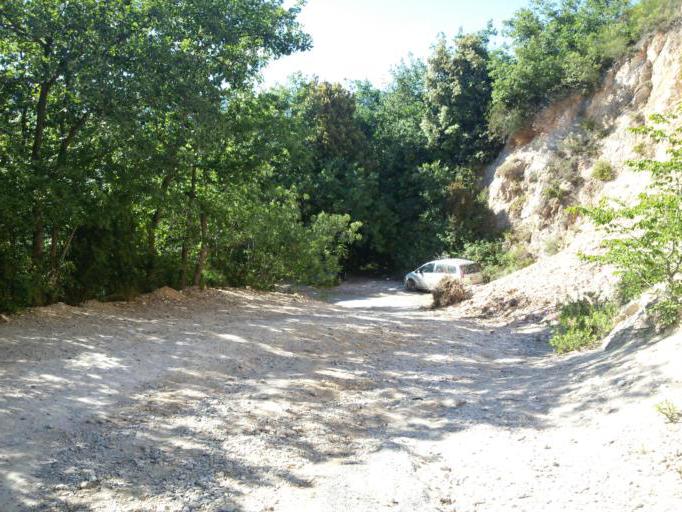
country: IT
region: Liguria
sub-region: Provincia di Savona
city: Calice Ligure
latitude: 44.1946
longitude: 8.3067
